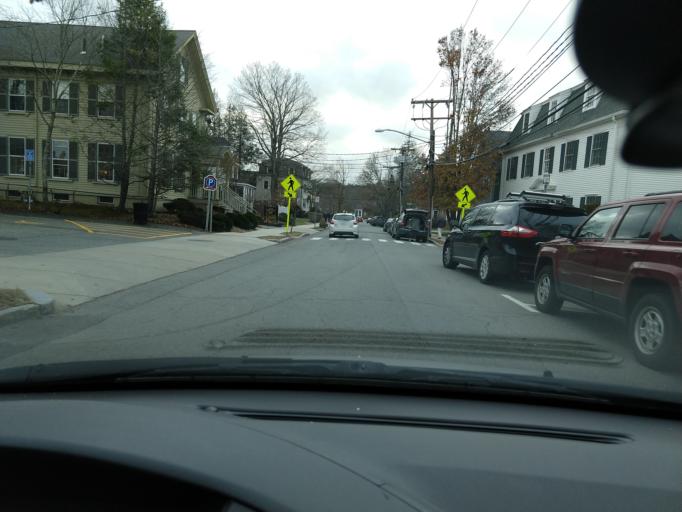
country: US
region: Massachusetts
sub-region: Middlesex County
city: Lexington
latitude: 42.4473
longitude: -71.2292
